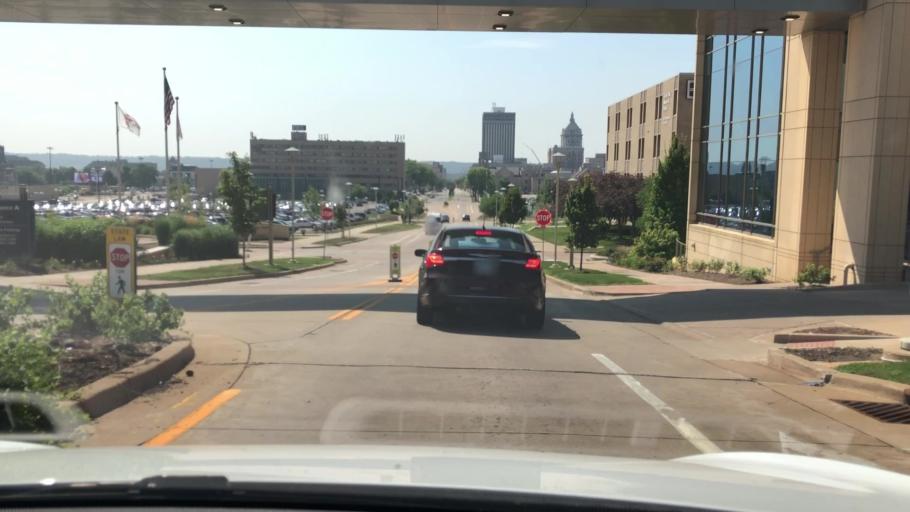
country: US
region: Illinois
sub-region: Peoria County
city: Peoria
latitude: 40.6999
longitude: -89.5960
